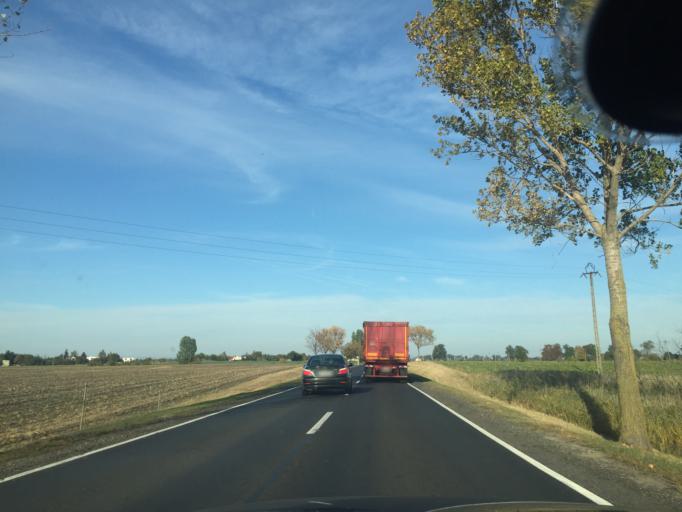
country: PL
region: Kujawsko-Pomorskie
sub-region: Powiat inowroclawski
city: Wierzchoslawice
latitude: 52.8632
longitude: 18.3588
